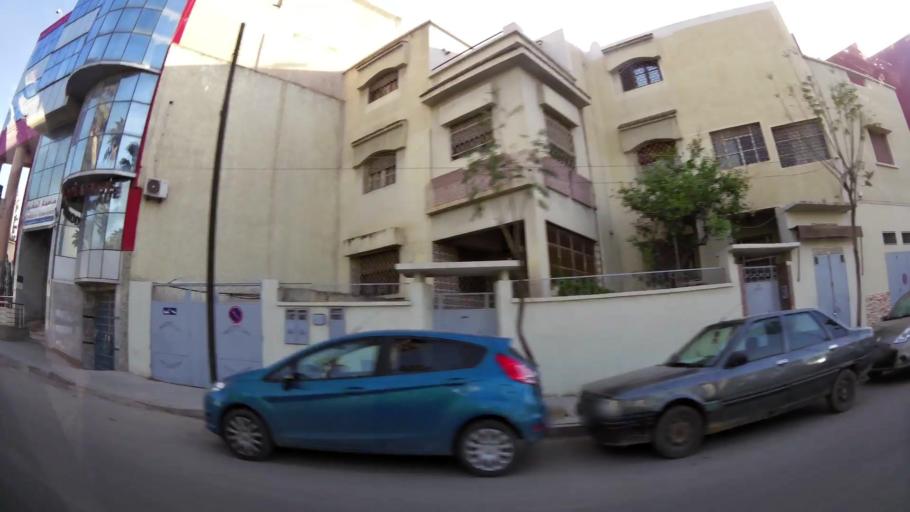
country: MA
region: Oriental
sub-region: Oujda-Angad
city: Oujda
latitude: 34.6764
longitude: -1.9167
